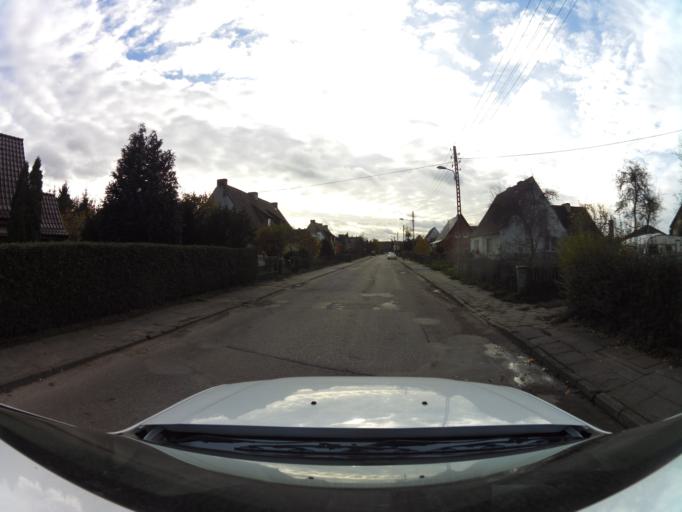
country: PL
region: West Pomeranian Voivodeship
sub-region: Powiat gryficki
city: Gryfice
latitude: 53.9183
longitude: 15.1812
